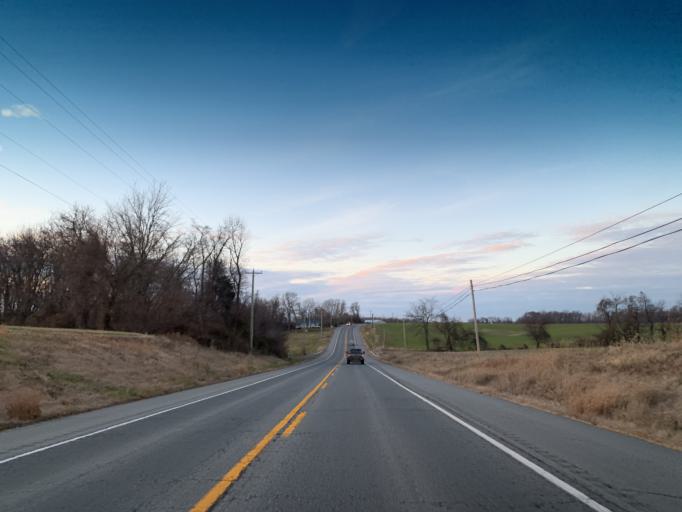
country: US
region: Delaware
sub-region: New Castle County
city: Middletown
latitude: 39.4432
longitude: -75.8662
